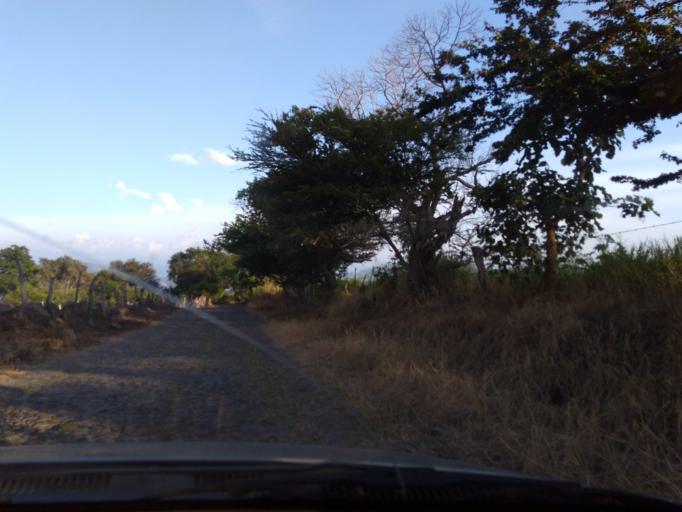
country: MX
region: Jalisco
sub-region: Tonila
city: San Marcos
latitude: 19.4607
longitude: -103.5243
